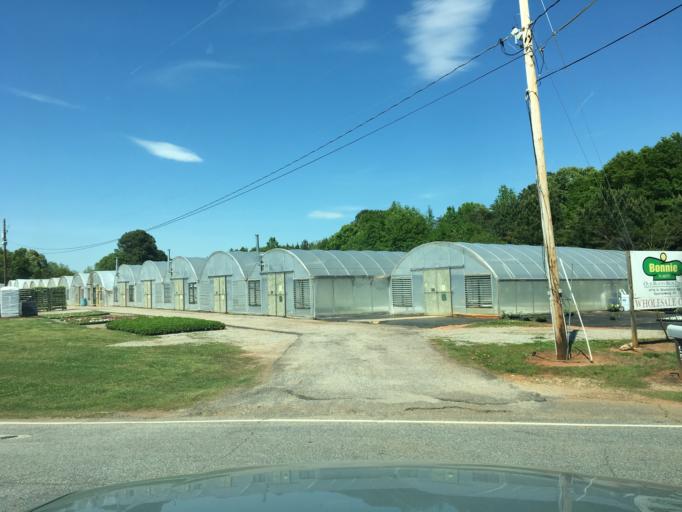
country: US
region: South Carolina
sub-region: Spartanburg County
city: Fairforest
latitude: 34.9695
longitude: -82.0328
